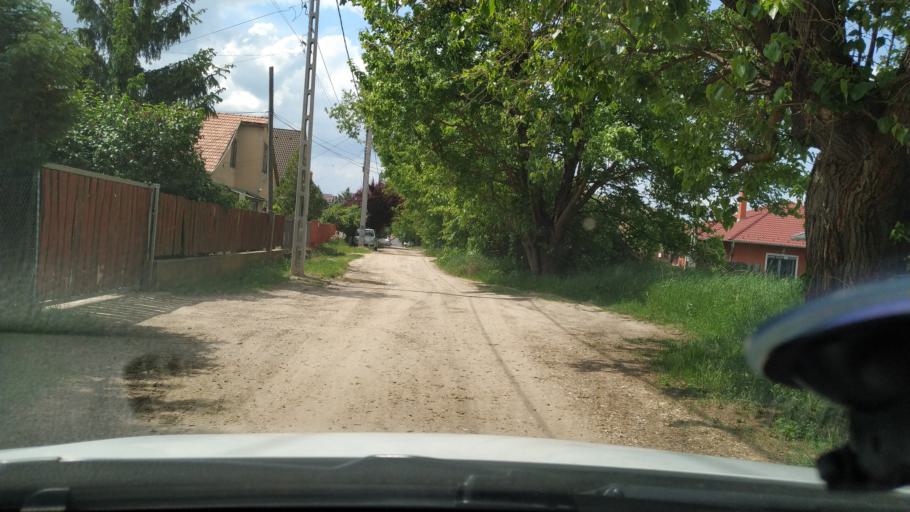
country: HU
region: Pest
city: Peteri
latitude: 47.4094
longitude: 19.4110
